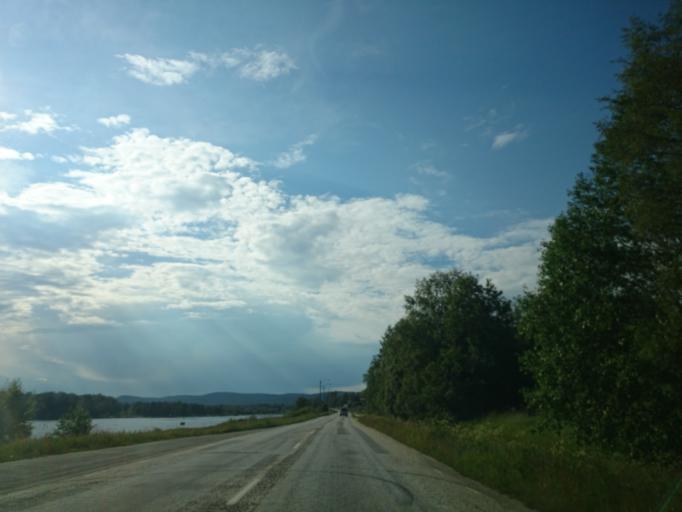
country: SE
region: Vaesternorrland
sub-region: Timra Kommun
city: Bergeforsen
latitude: 62.5465
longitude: 17.4414
